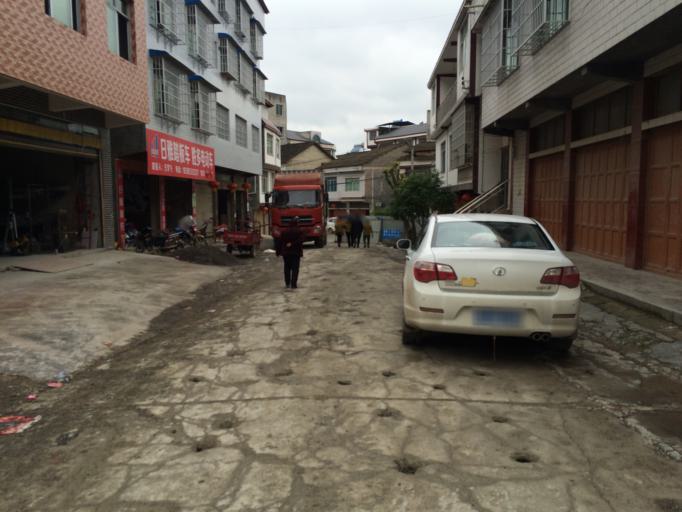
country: CN
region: Guizhou Sheng
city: Dalucao
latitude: 27.8339
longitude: 107.2529
